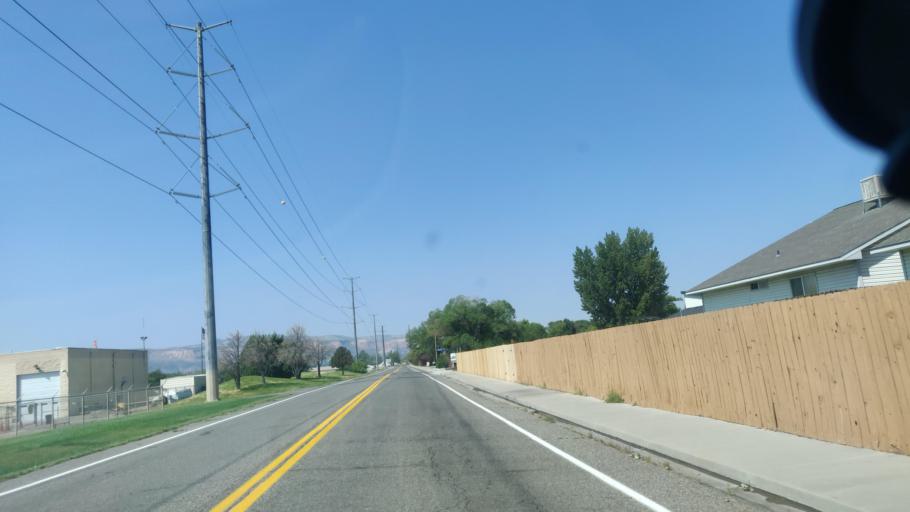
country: US
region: Colorado
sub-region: Mesa County
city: Grand Junction
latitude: 39.0991
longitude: -108.5836
